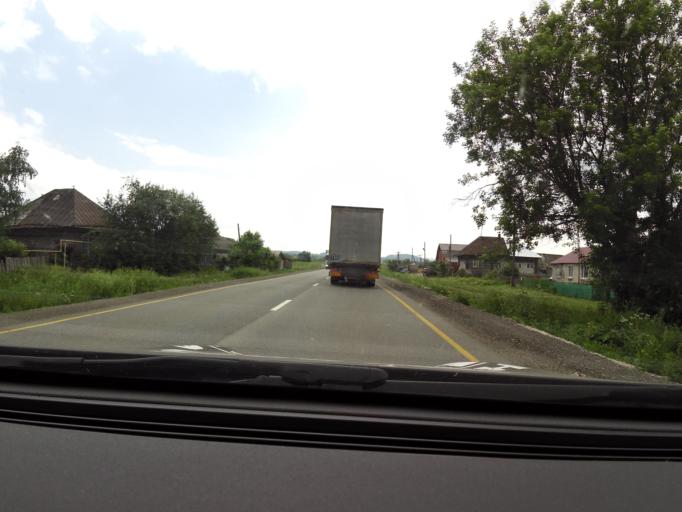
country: RU
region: Perm
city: Suksun
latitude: 57.0560
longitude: 57.4254
